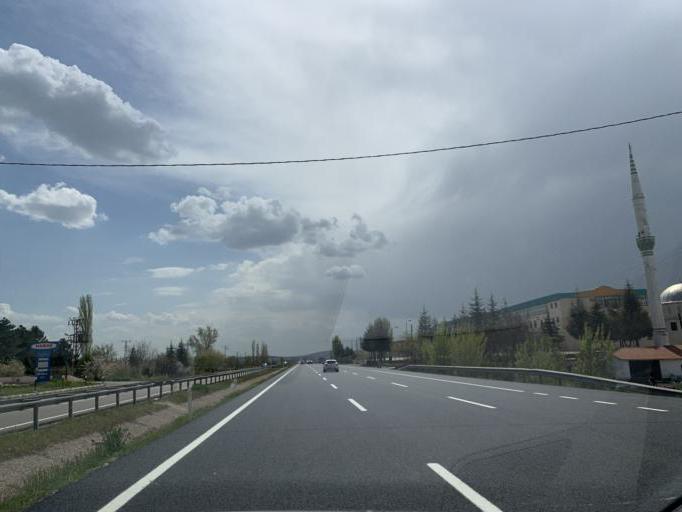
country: TR
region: Ankara
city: Polatli
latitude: 39.6722
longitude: 32.2321
